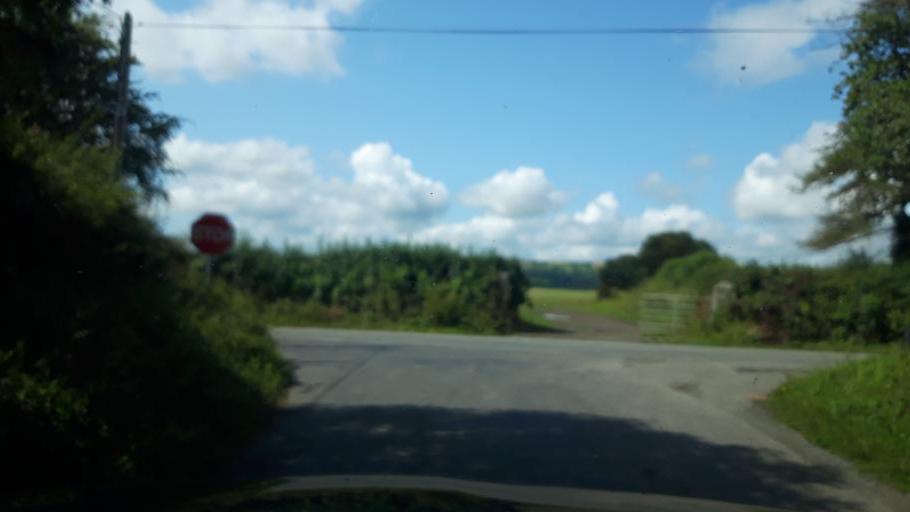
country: IE
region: Leinster
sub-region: Kilkenny
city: Graiguenamanagh
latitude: 52.5589
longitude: -6.9821
